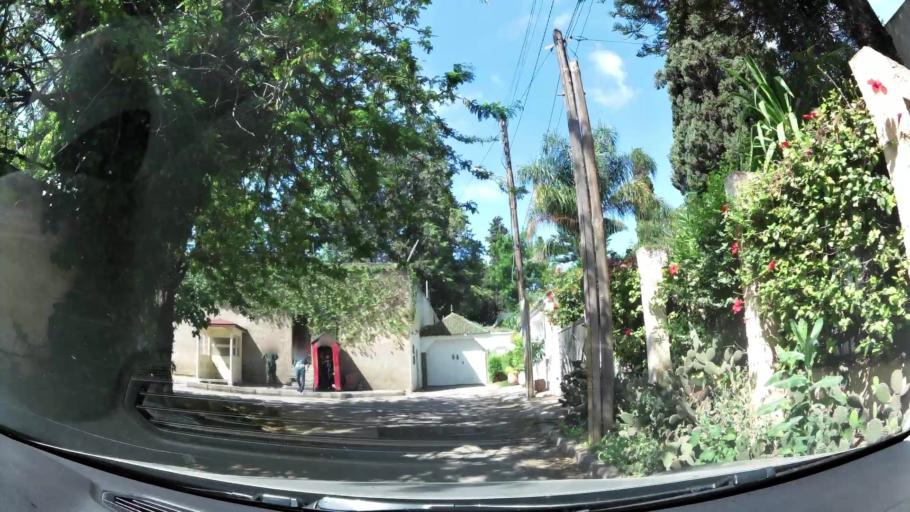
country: MA
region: Fes-Boulemane
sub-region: Fes
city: Fes
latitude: 34.0314
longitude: -5.0190
